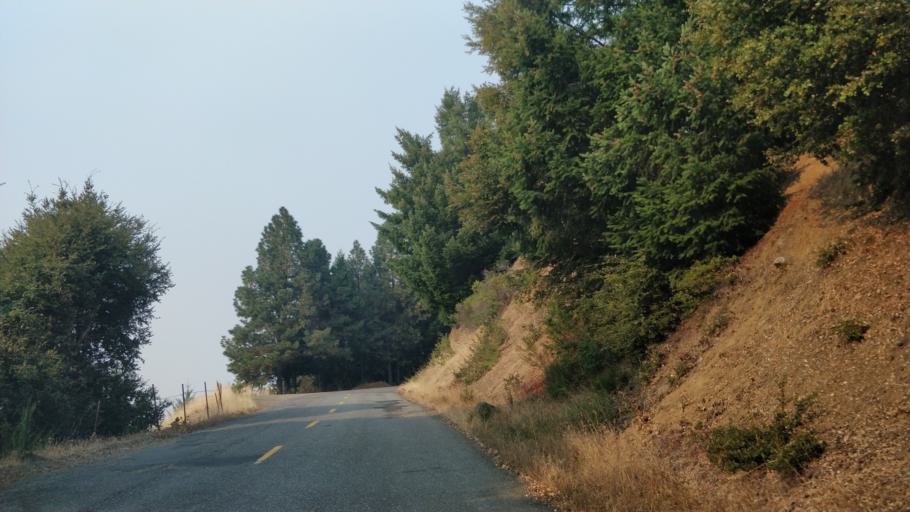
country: US
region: California
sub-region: Humboldt County
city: Rio Dell
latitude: 40.2606
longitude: -124.1155
